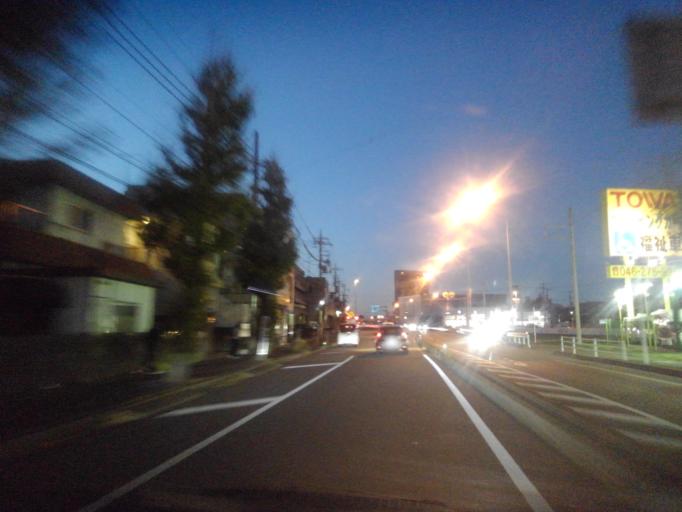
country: JP
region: Tokyo
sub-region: Machida-shi
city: Machida
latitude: 35.5140
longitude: 139.4575
